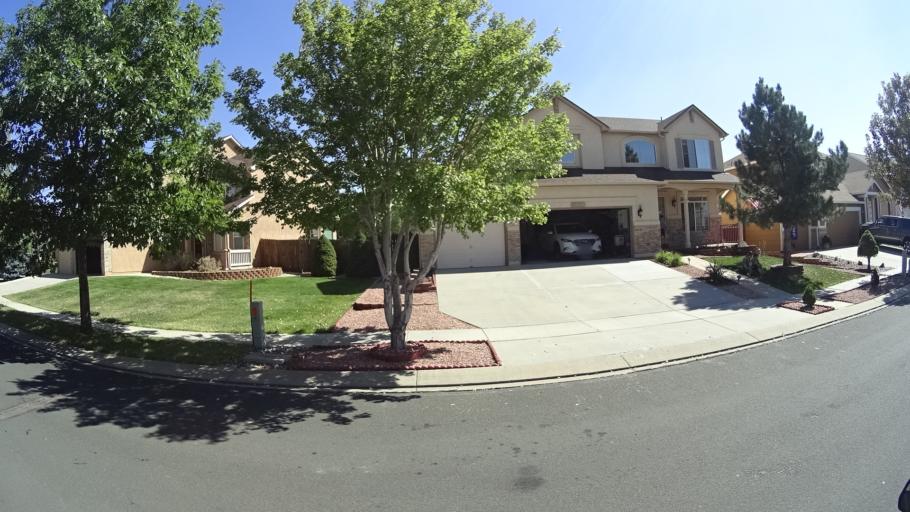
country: US
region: Colorado
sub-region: El Paso County
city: Cimarron Hills
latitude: 38.8962
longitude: -104.7054
